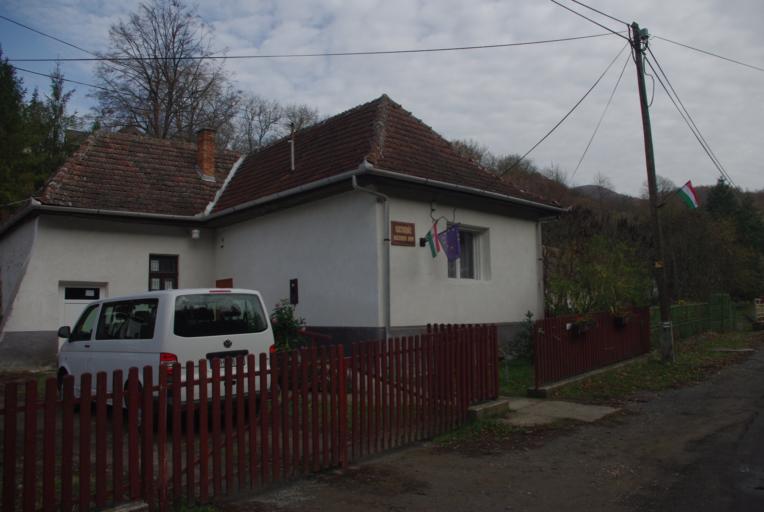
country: HU
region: Borsod-Abauj-Zemplen
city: Sarospatak
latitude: 48.4231
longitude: 21.5393
